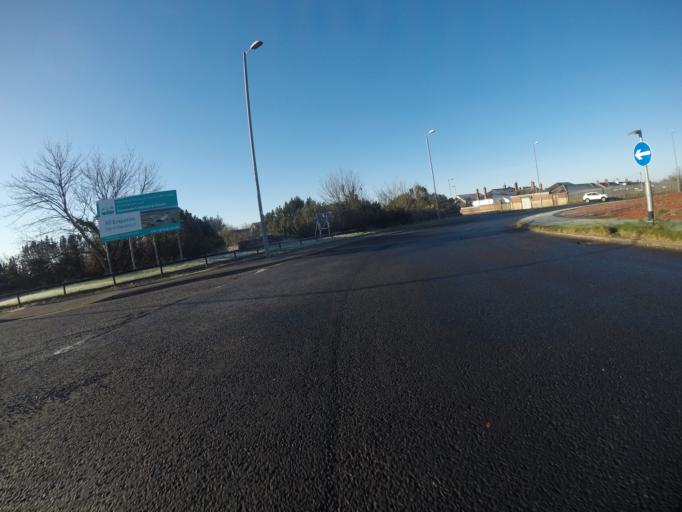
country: GB
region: Scotland
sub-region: North Ayrshire
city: Stevenston
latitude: 55.6342
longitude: -4.7435
